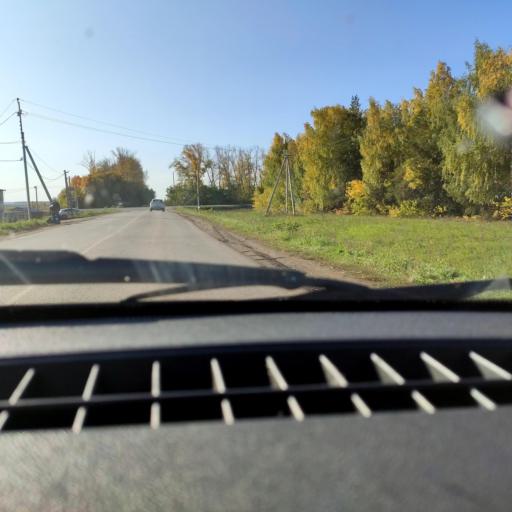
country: RU
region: Bashkortostan
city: Avdon
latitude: 54.5904
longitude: 55.8009
